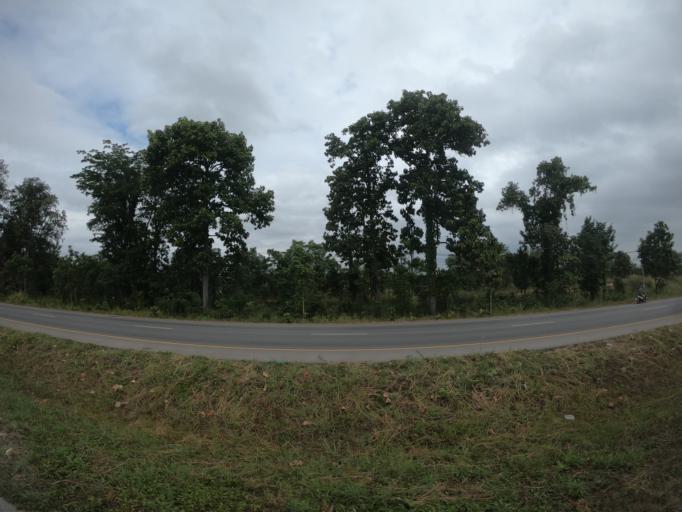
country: TH
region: Maha Sarakham
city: Kut Rang
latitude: 16.0461
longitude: 102.8934
